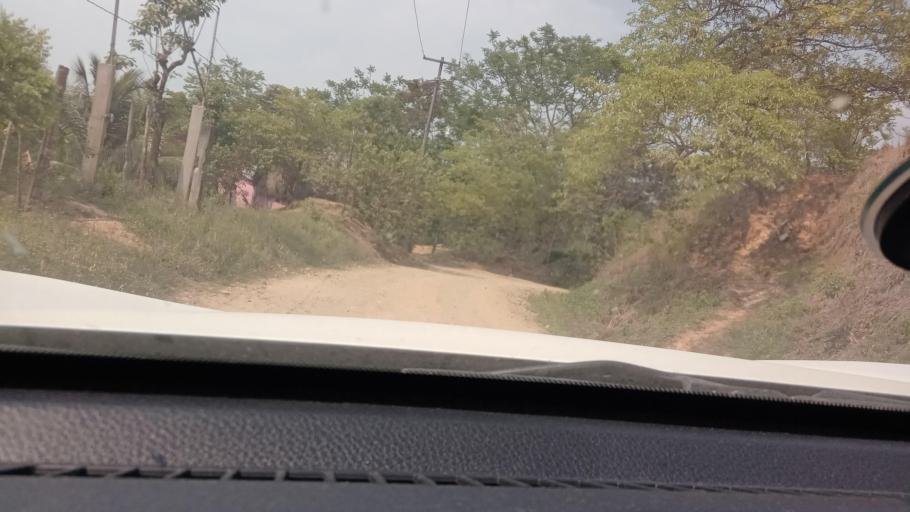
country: MX
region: Tabasco
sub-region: Huimanguillo
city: Francisco Rueda
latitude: 17.6762
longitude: -93.8667
